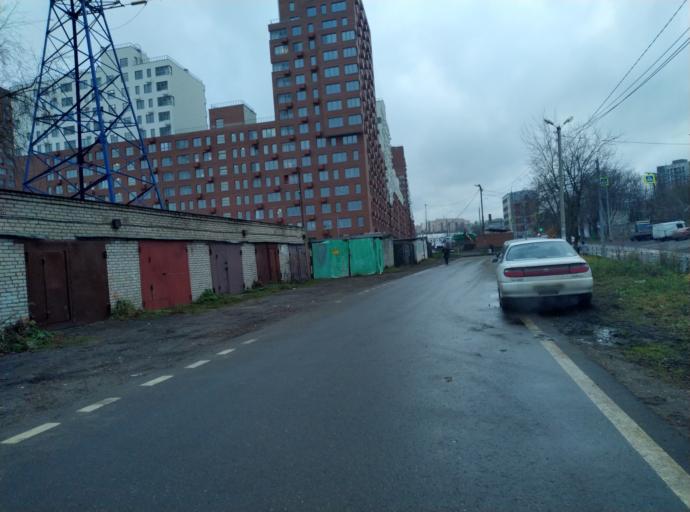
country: RU
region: Moskovskaya
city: Korenevo
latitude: 55.6669
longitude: 37.9981
